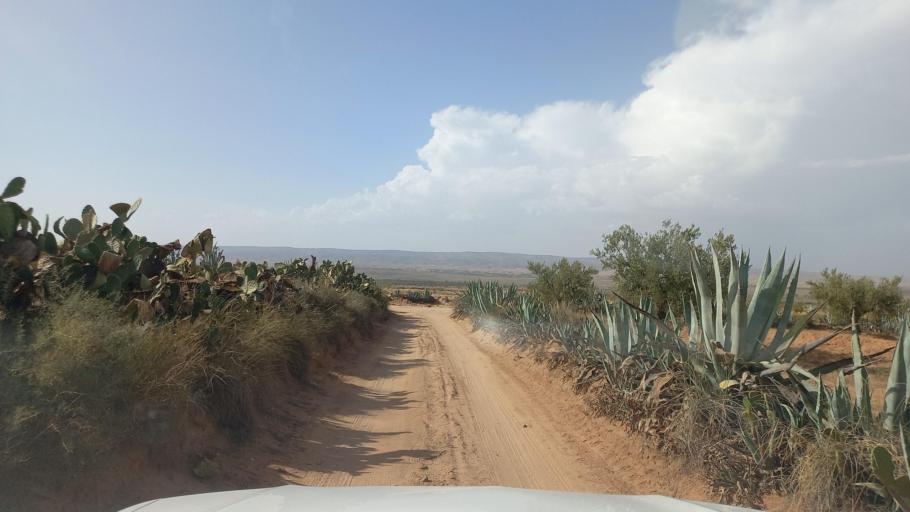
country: TN
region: Al Qasrayn
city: Kasserine
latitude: 35.2080
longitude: 8.9674
